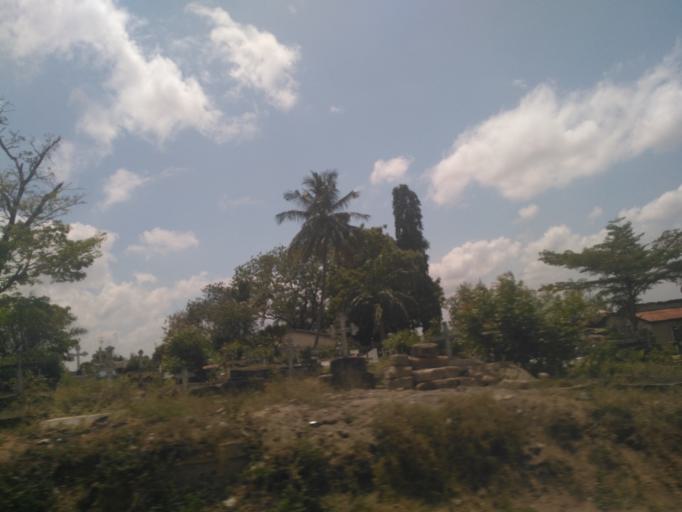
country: TZ
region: Dar es Salaam
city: Dar es Salaam
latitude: -6.8866
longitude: 39.2706
